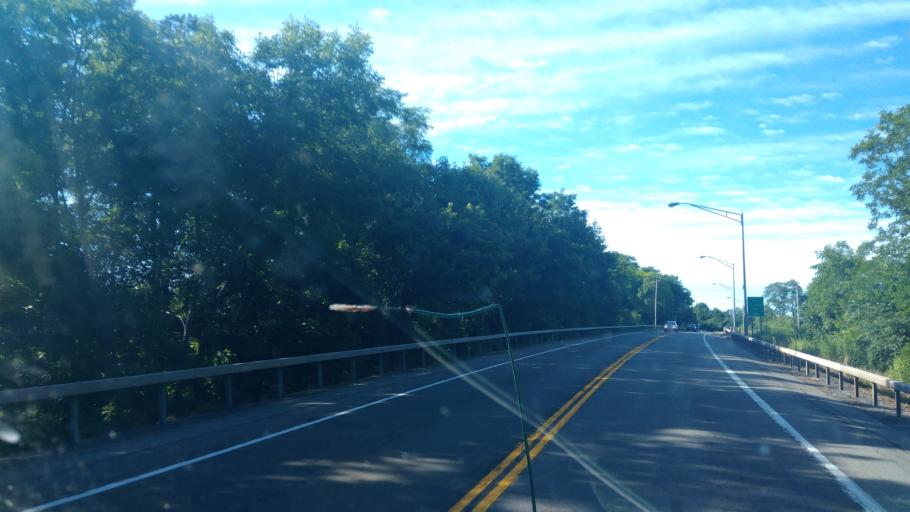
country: US
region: New York
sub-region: Wayne County
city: Lyons
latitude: 43.0549
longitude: -76.9934
